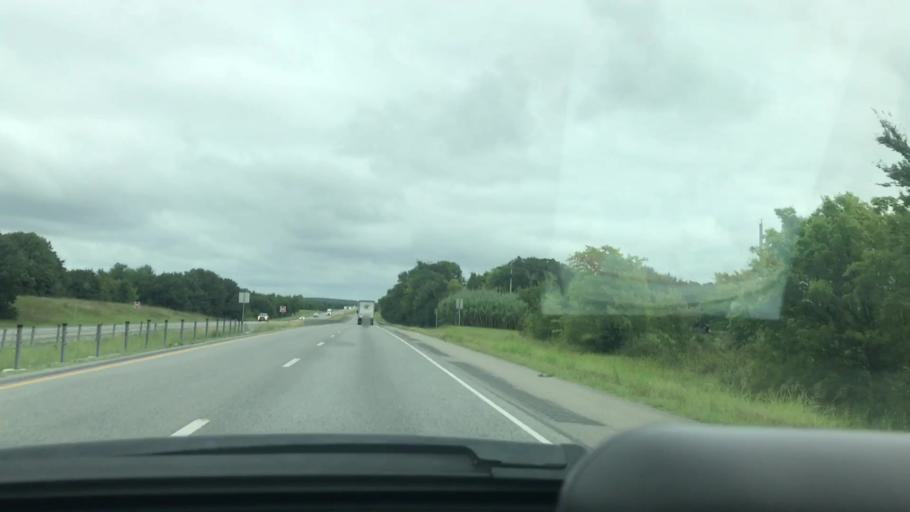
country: US
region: Oklahoma
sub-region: Pittsburg County
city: McAlester
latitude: 34.7627
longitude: -95.8895
